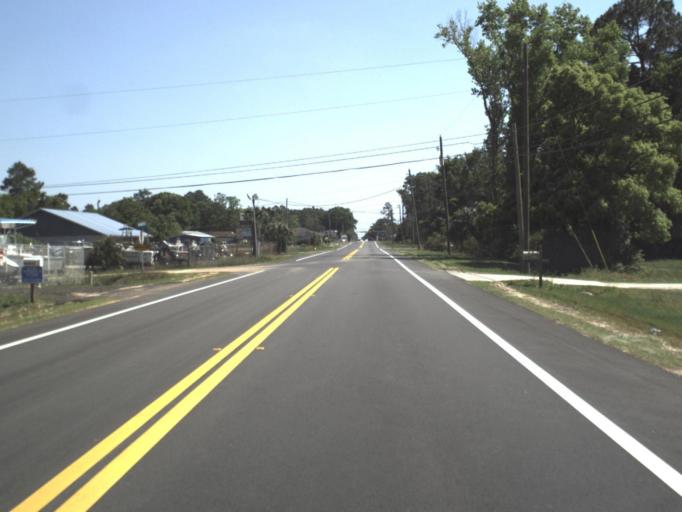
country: US
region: Florida
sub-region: Bay County
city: Hiland Park
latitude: 30.2036
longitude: -85.6078
